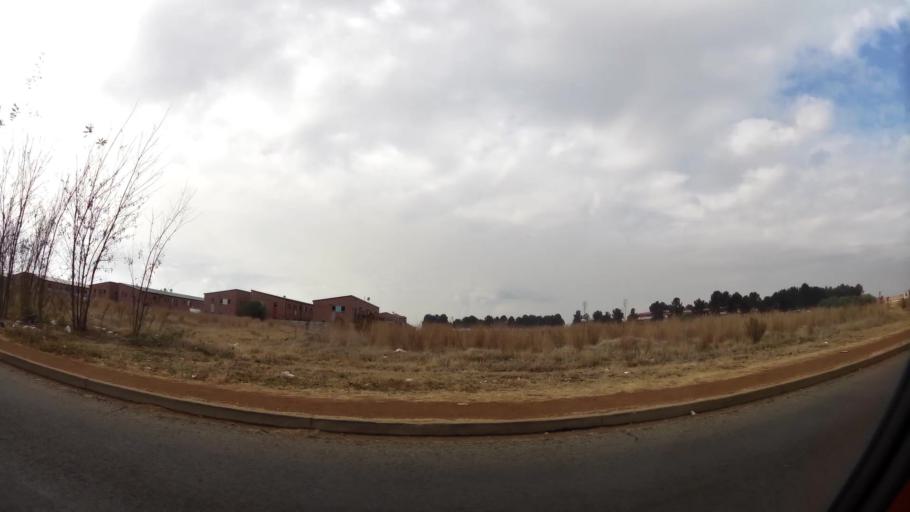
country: ZA
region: Gauteng
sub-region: Sedibeng District Municipality
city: Vanderbijlpark
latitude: -26.7198
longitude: 27.8628
